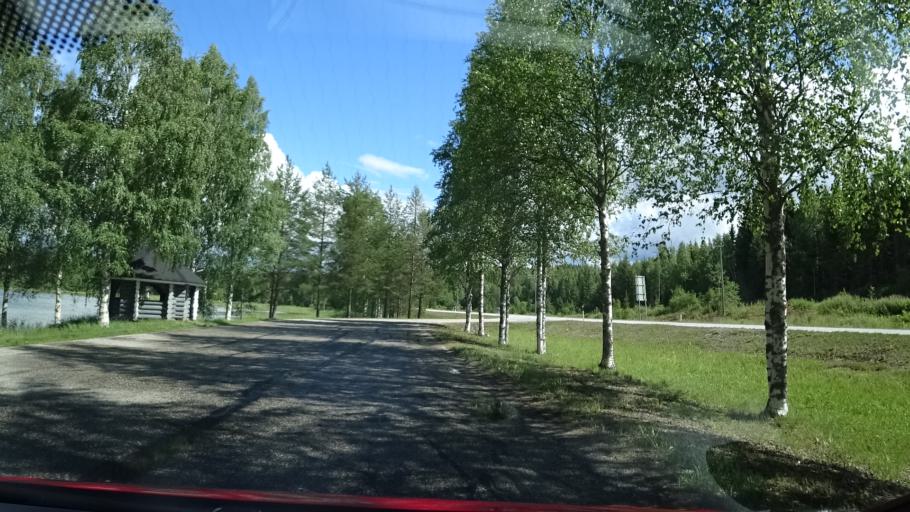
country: FI
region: North Karelia
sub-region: Pielisen Karjala
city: Nurmes
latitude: 63.5529
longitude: 28.9909
